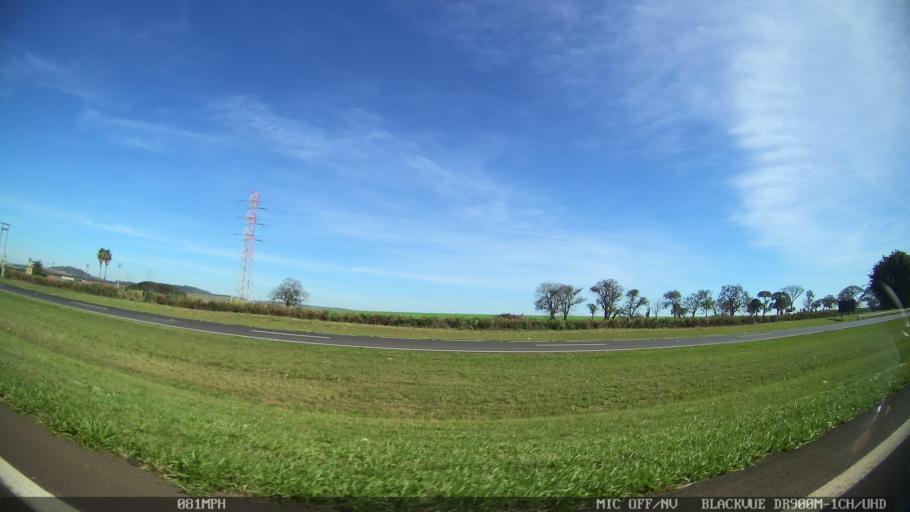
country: BR
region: Sao Paulo
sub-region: Araras
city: Araras
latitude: -22.2847
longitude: -47.3934
